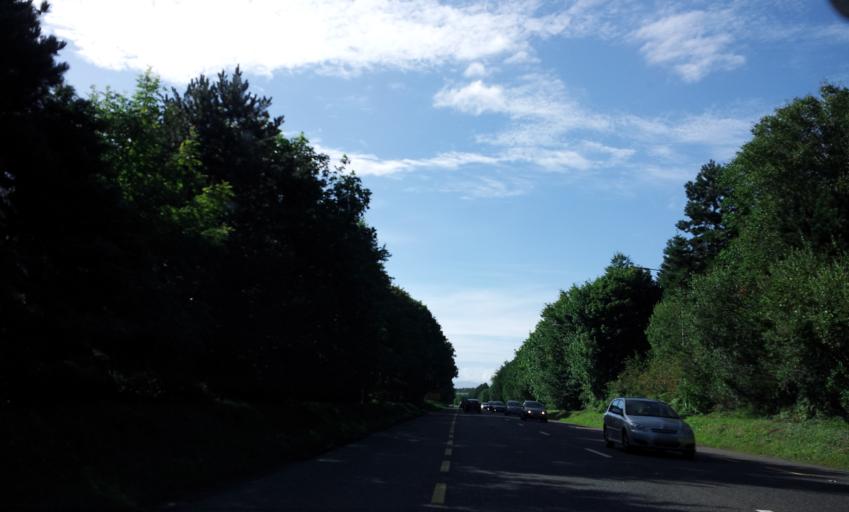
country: IE
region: Munster
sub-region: Ciarrai
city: Cill Airne
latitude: 52.0645
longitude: -9.4899
